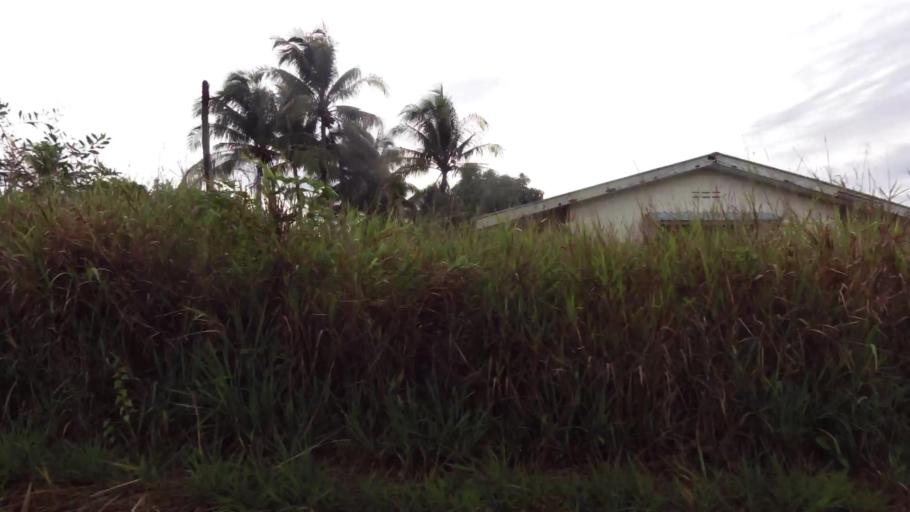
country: BN
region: Belait
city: Seria
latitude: 4.6051
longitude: 114.3304
